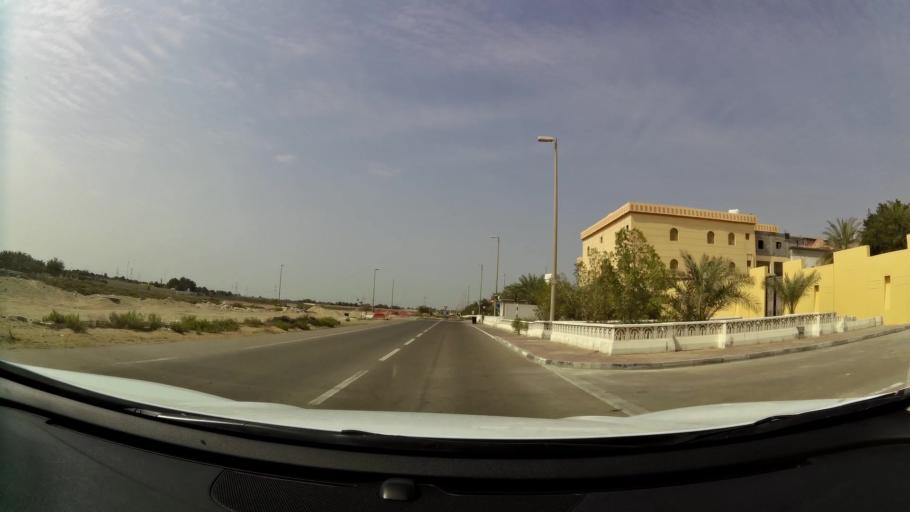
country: AE
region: Abu Dhabi
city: Abu Dhabi
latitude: 24.5411
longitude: 54.6668
